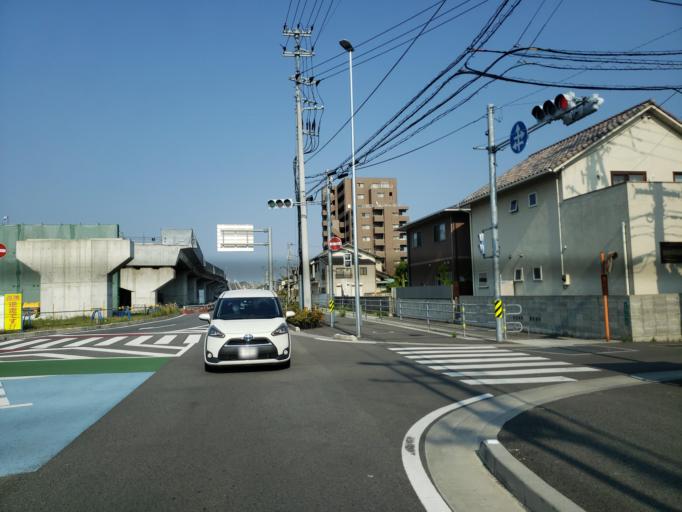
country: JP
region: Ehime
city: Masaki-cho
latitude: 33.8111
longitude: 132.7264
